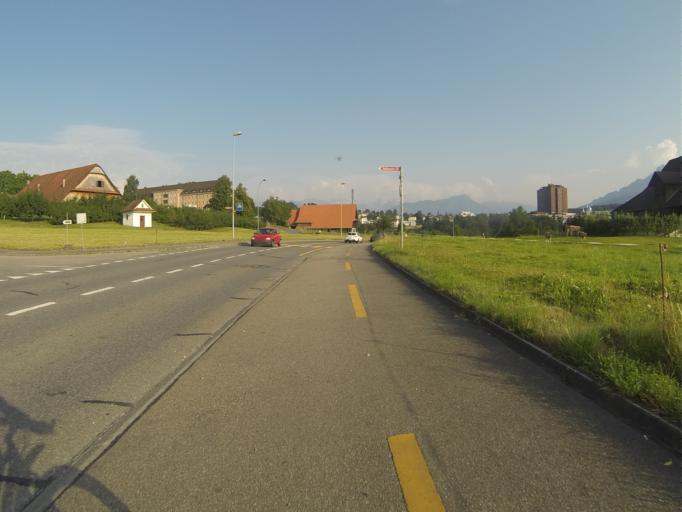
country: CH
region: Lucerne
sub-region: Lucerne-Stadt District
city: Luzern
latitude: 47.0662
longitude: 8.2970
